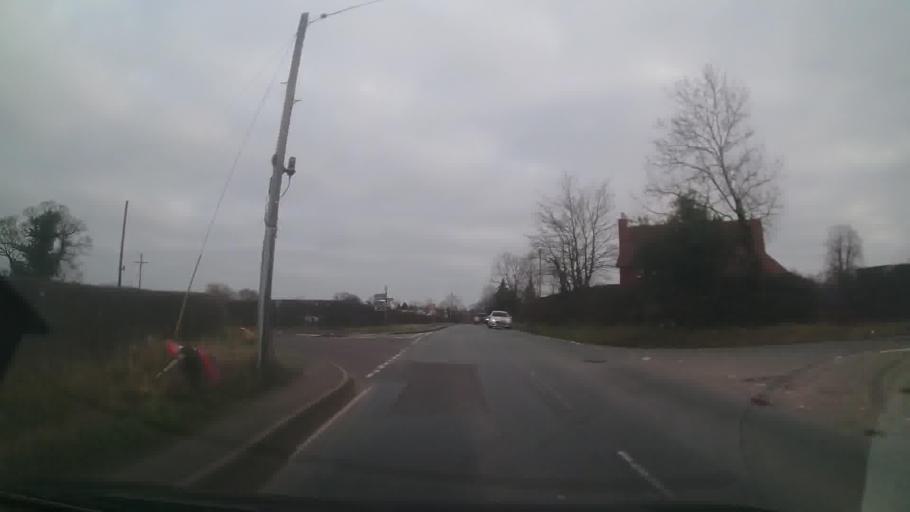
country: GB
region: England
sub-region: Shropshire
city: Bicton
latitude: 52.7739
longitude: -2.8199
